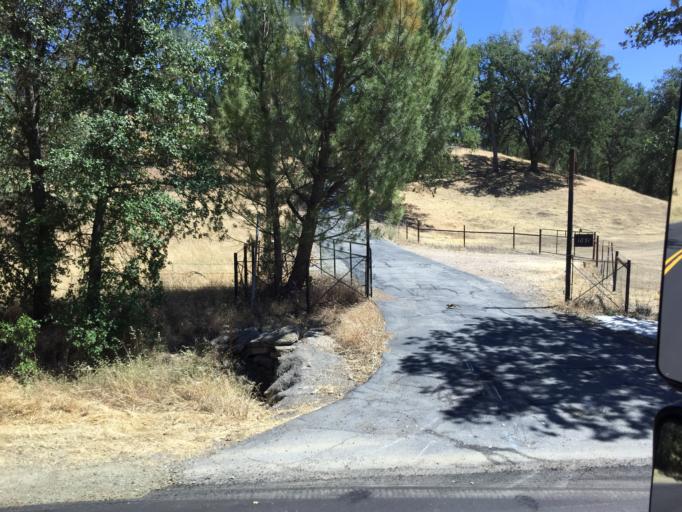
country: US
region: California
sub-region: San Luis Obispo County
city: Santa Margarita
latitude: 35.2992
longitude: -120.4012
